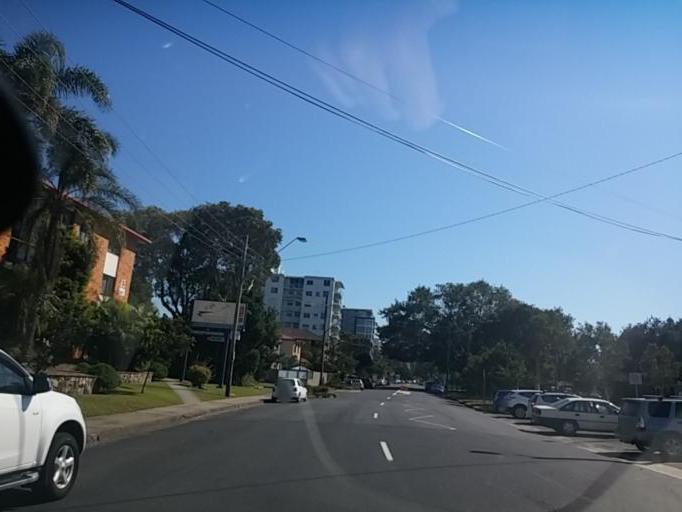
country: AU
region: New South Wales
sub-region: Coffs Harbour
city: Coffs Harbour
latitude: -30.2885
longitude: 153.1381
